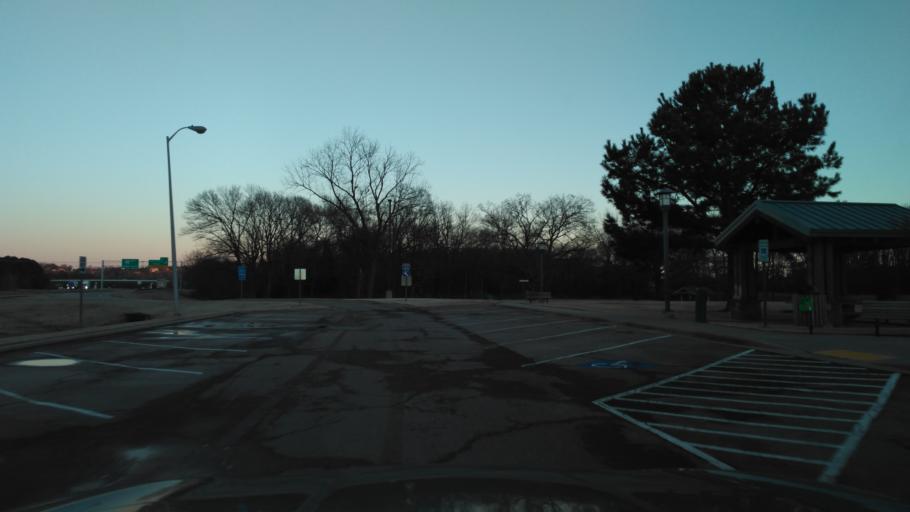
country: US
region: Arkansas
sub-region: Crawford County
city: Van Buren
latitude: 35.4589
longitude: -94.3984
